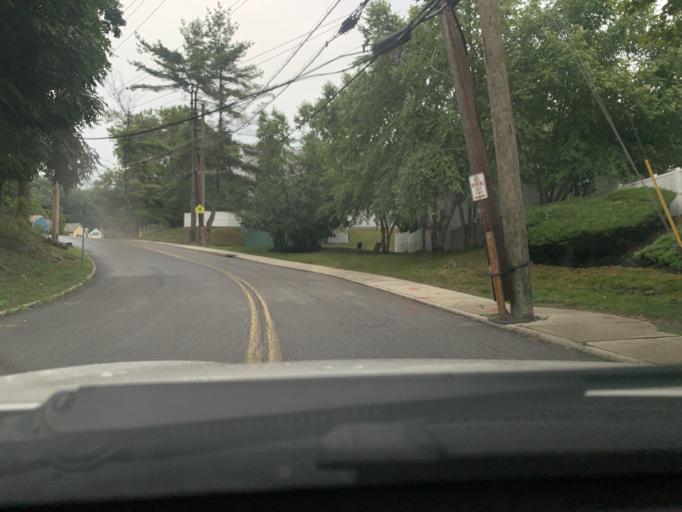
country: US
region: New York
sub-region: Westchester County
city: Ossining
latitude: 41.1689
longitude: -73.8621
